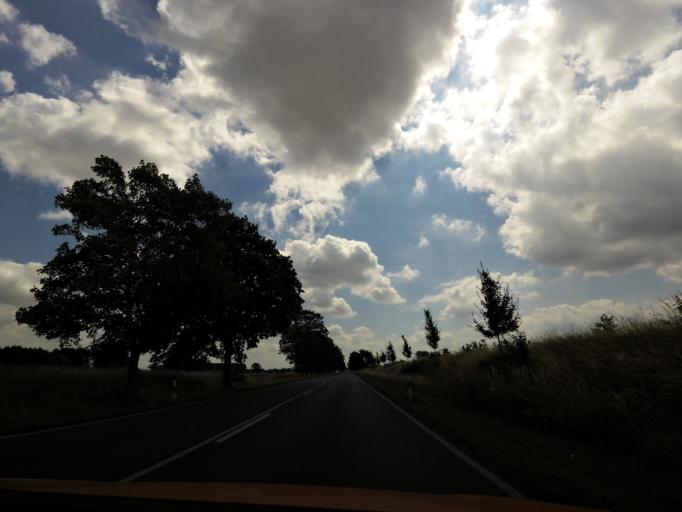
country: DE
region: Brandenburg
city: Wusterhausen
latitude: 52.8766
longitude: 12.4711
